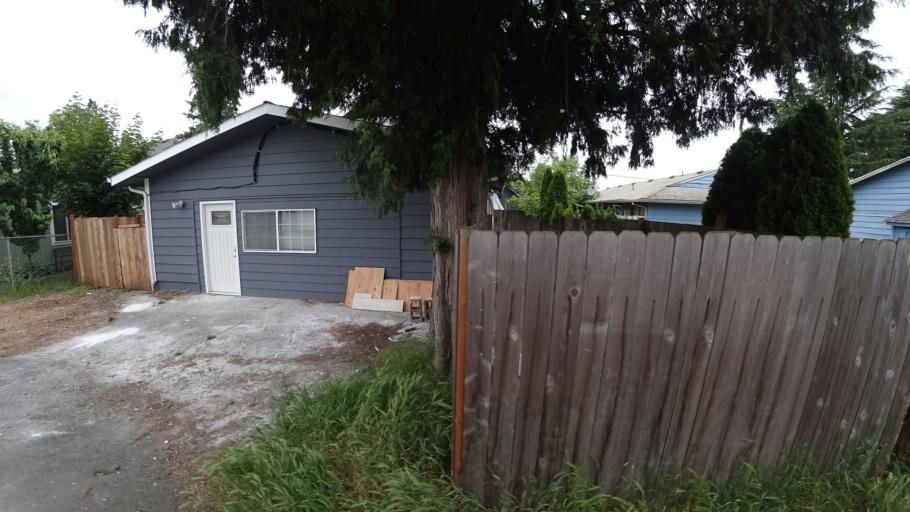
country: US
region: Oregon
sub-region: Multnomah County
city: Lents
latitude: 45.4827
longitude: -122.5730
